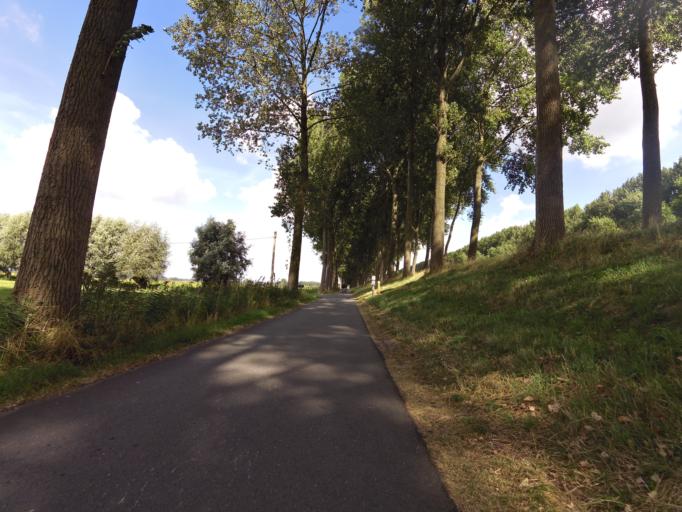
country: BE
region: Flanders
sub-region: Provincie West-Vlaanderen
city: Damme
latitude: 51.2423
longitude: 3.2680
